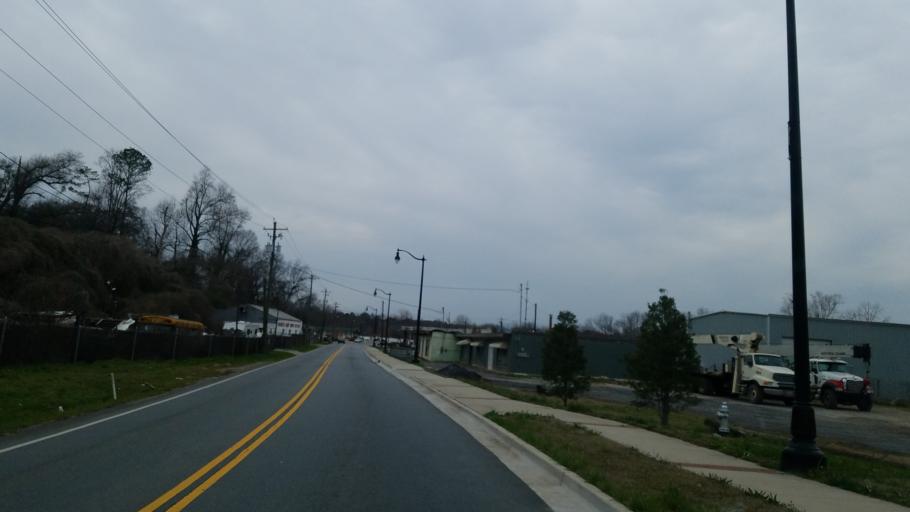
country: US
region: Georgia
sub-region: Cherokee County
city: Canton
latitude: 34.2281
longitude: -84.4891
